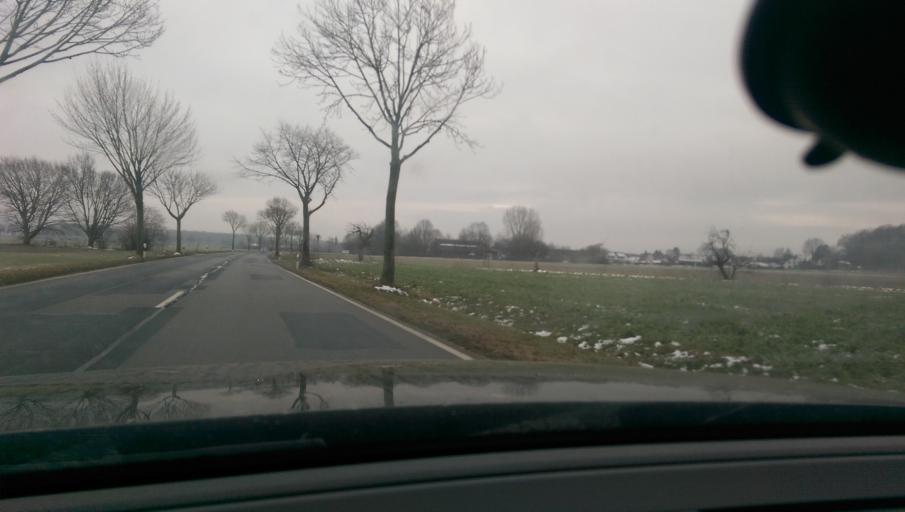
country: DE
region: Lower Saxony
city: Grossgoltern
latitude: 52.3478
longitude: 9.5493
